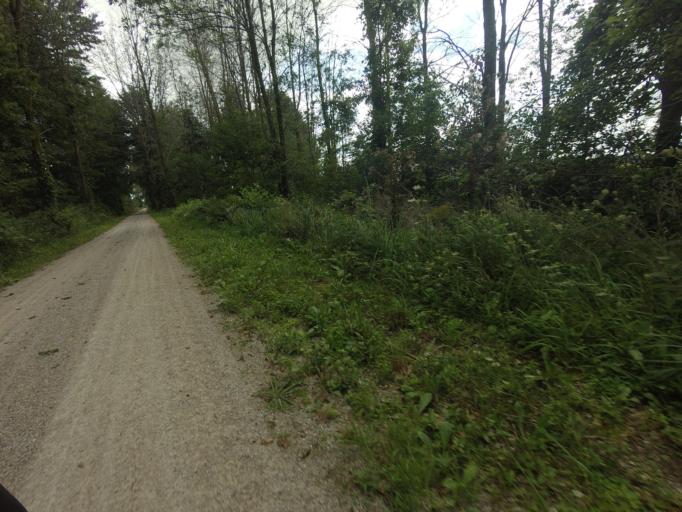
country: CA
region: Ontario
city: North Perth
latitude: 43.5941
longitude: -81.0912
